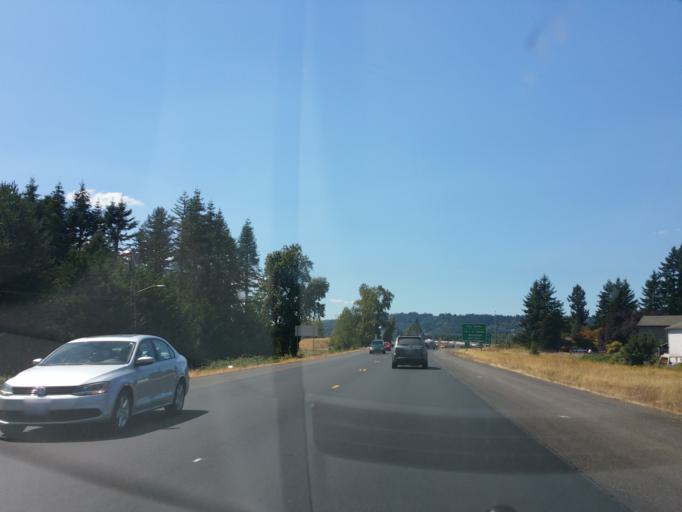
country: US
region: Washington
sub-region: Clark County
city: Washougal
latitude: 45.5785
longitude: -122.3656
